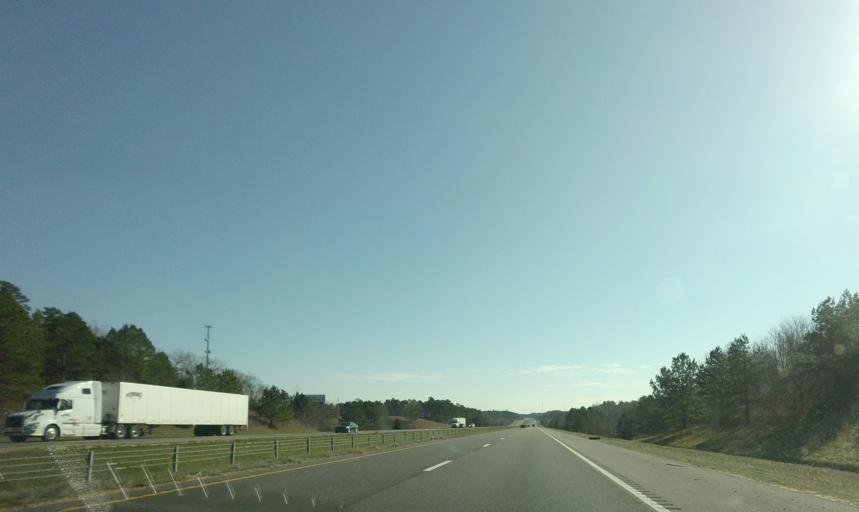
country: US
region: Mississippi
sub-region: Union County
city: New Albany
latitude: 34.5824
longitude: -89.1639
